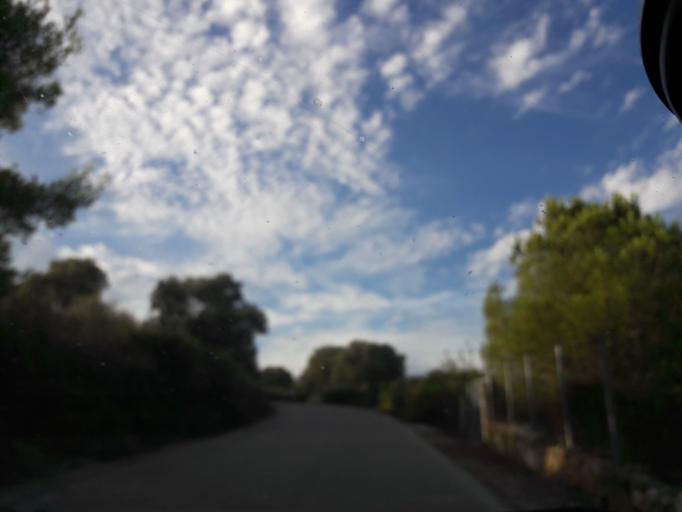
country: GR
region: Central Macedonia
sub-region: Nomos Chalkidikis
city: Nea Roda
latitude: 40.3333
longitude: 23.8987
